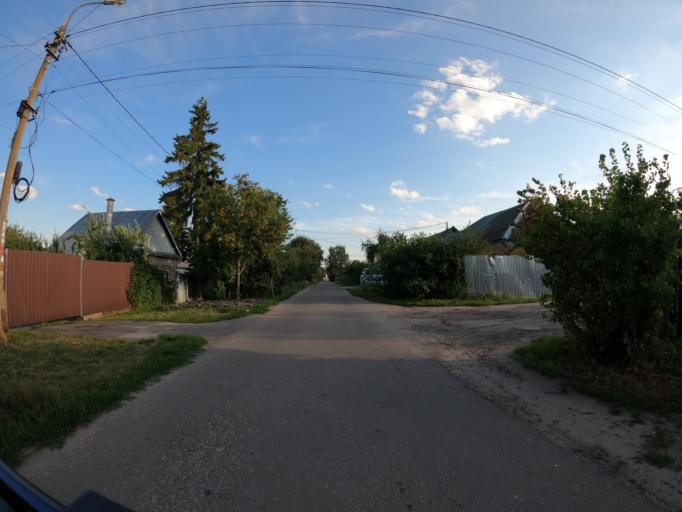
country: RU
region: Moskovskaya
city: Raduzhnyy
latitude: 55.1044
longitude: 38.7253
